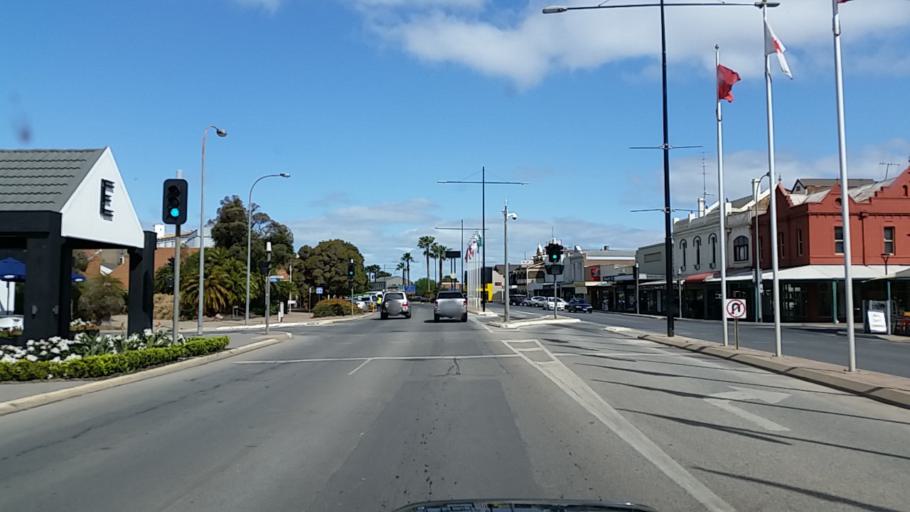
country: AU
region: South Australia
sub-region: Port Pirie City and Dists
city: Port Pirie
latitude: -33.1766
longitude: 138.0102
